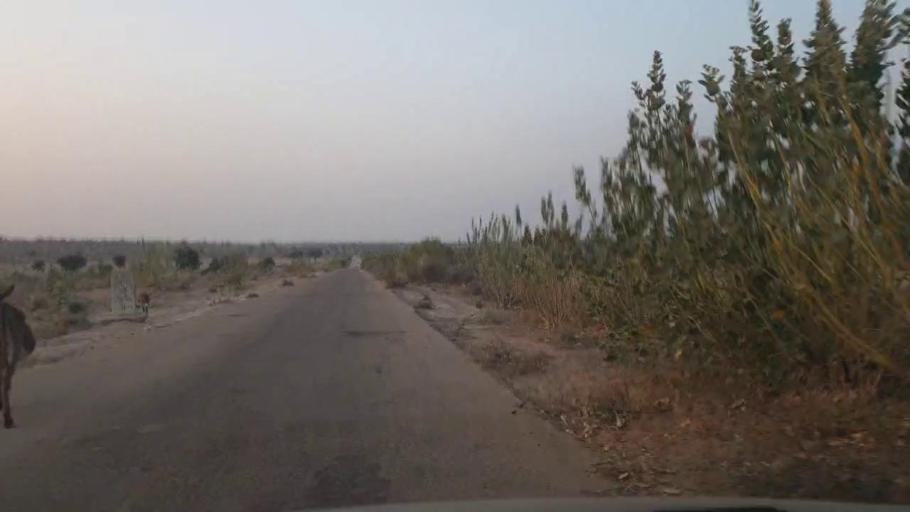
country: PK
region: Sindh
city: Umarkot
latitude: 25.2997
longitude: 70.0738
